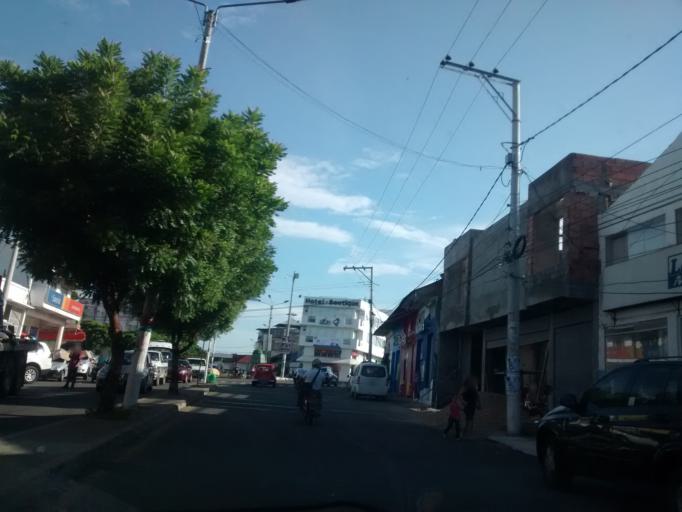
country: CO
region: Cundinamarca
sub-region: Girardot
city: Girardot City
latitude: 4.2983
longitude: -74.8040
